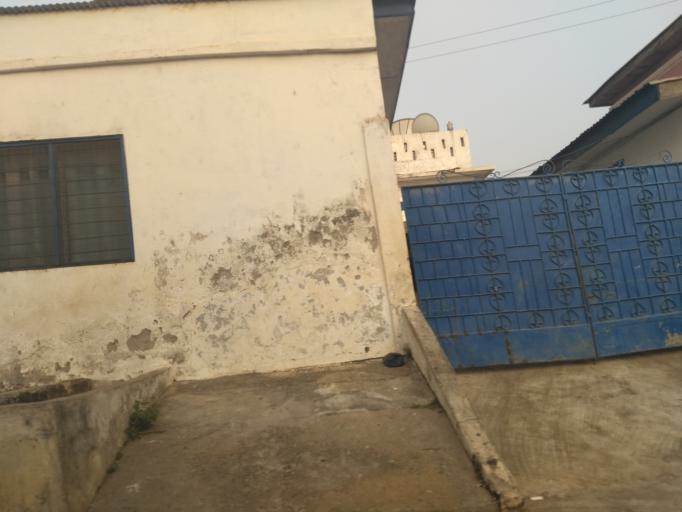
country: GH
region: Ashanti
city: Kumasi
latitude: 6.6846
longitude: -1.6124
